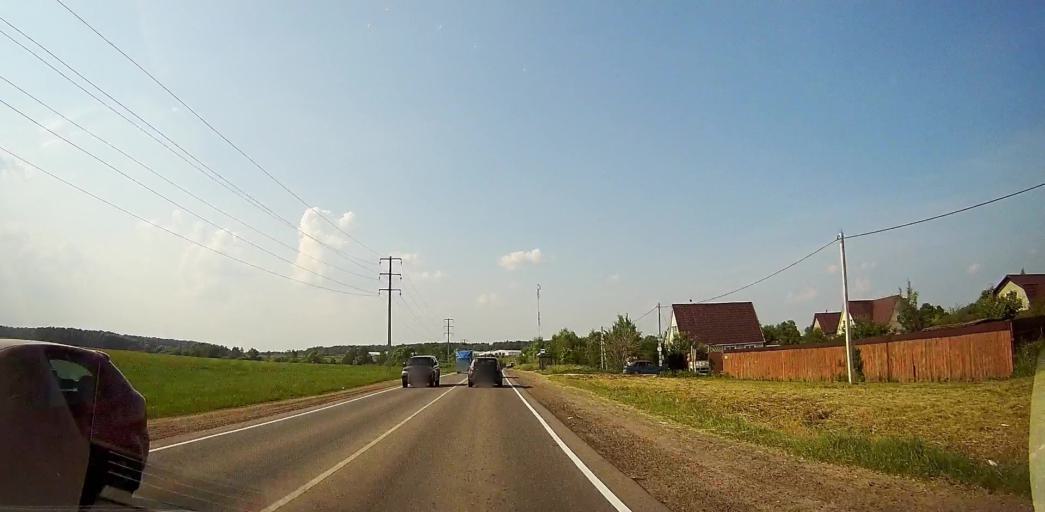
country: RU
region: Moskovskaya
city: Barybino
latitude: 55.2982
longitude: 37.9118
